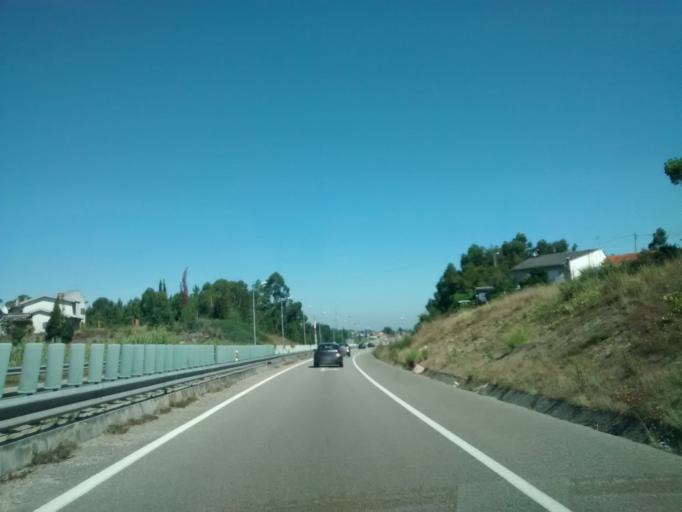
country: PT
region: Aveiro
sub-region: Oliveira do Bairro
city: Oliveira do Bairro
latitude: 40.5190
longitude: -8.5039
